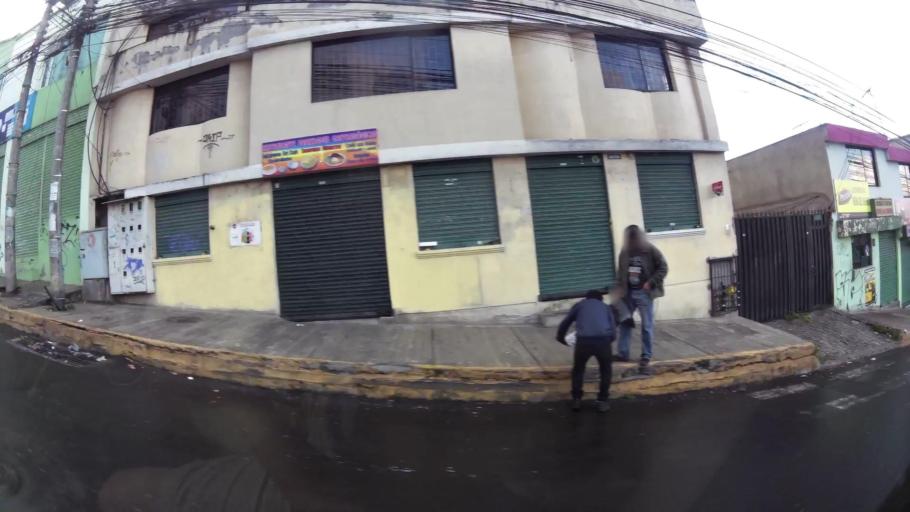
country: EC
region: Pichincha
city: Quito
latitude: -0.1125
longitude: -78.5086
